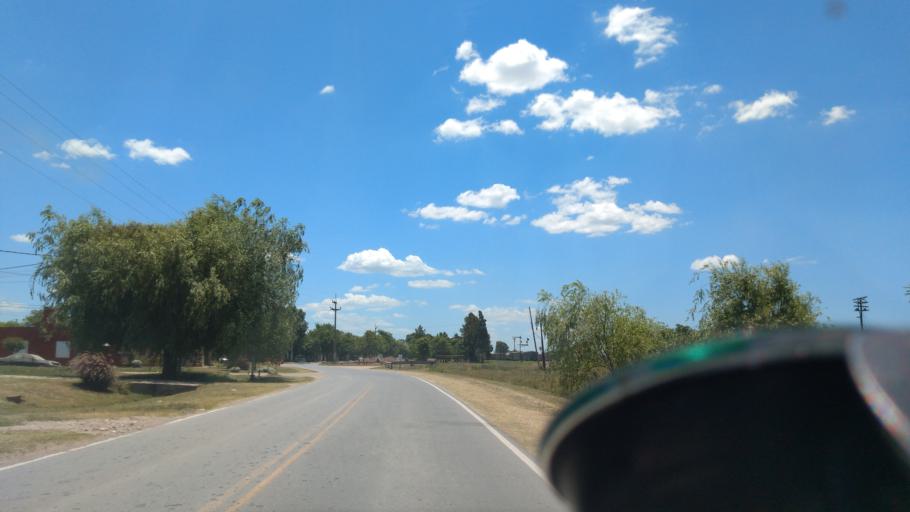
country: AR
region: Santa Fe
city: Laguna Paiva
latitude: -31.3152
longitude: -60.6584
